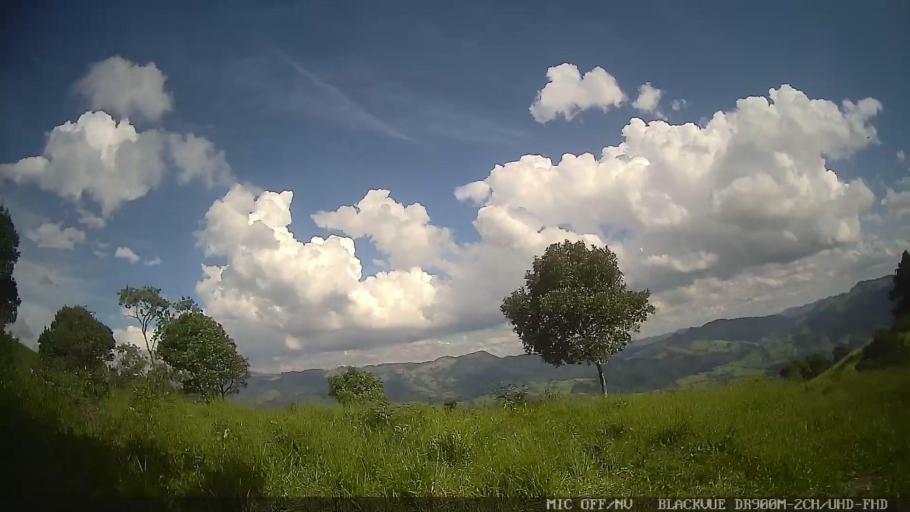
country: BR
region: Minas Gerais
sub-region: Extrema
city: Extrema
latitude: -22.8177
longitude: -46.2514
